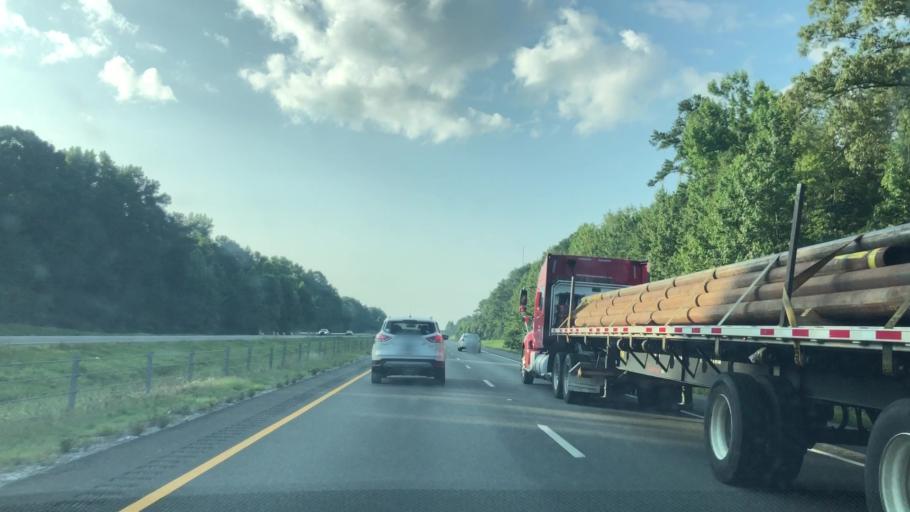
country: US
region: Alabama
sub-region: Chilton County
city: Clanton
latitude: 32.8705
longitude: -86.6117
